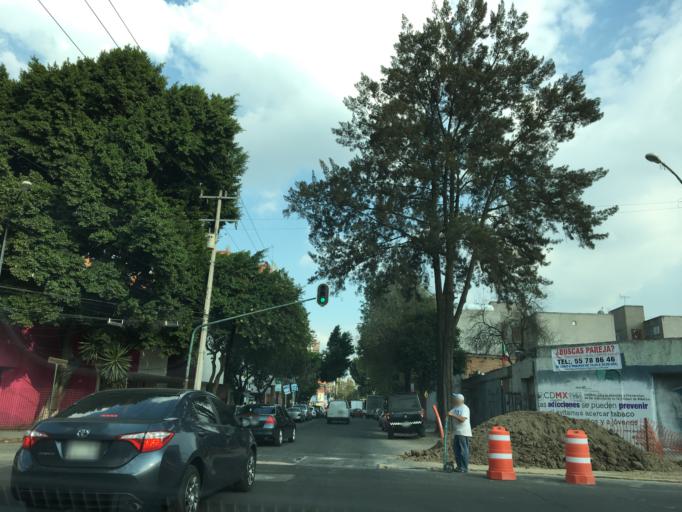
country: MX
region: Mexico City
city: Benito Juarez
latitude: 19.4181
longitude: -99.1478
